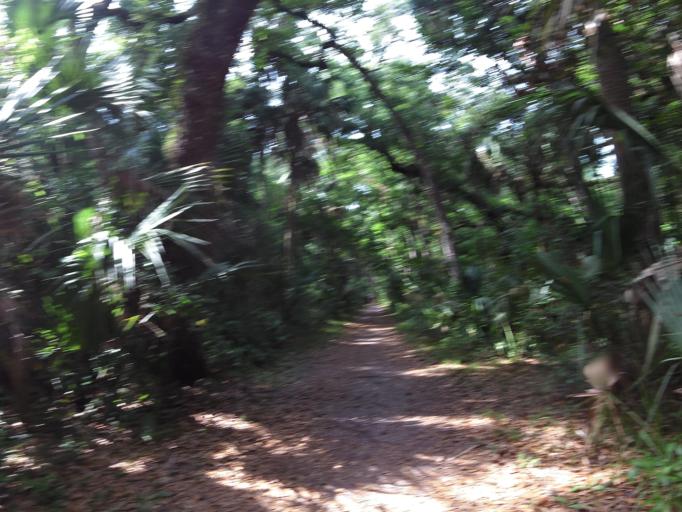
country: US
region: Florida
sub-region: Flagler County
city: Palm Coast
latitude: 29.6352
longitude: -81.2102
